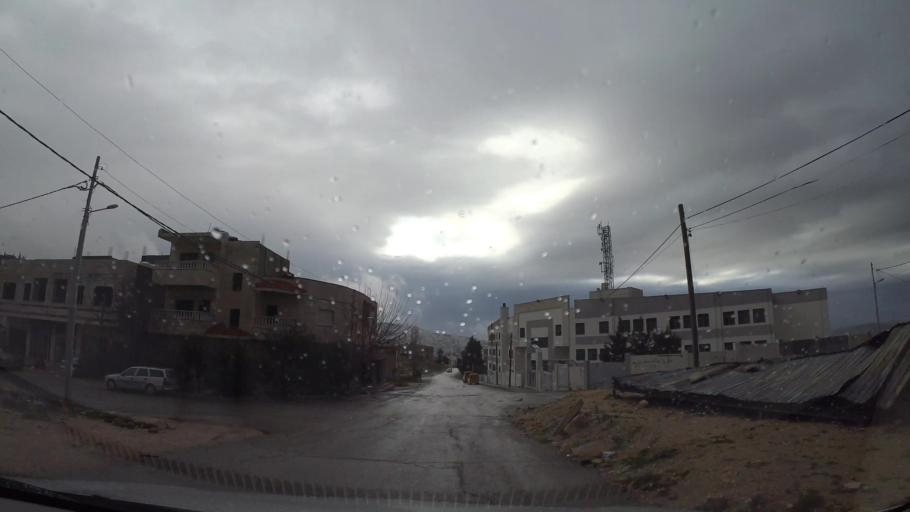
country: JO
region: Amman
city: Al Jubayhah
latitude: 32.0415
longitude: 35.8428
